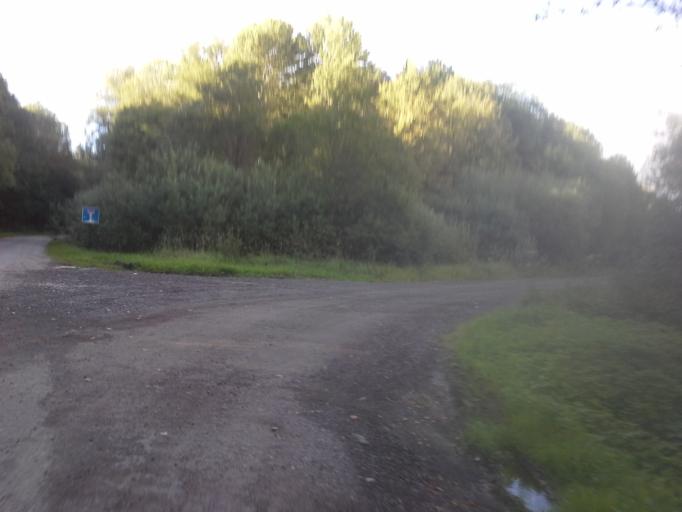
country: RU
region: Moskovskaya
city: Kievskij
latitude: 55.4433
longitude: 36.8222
